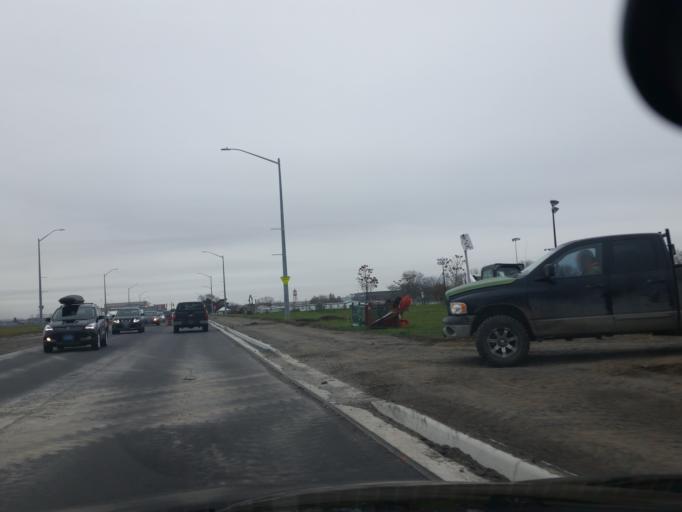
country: CA
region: Ontario
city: Quinte West
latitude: 44.1055
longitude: -77.5513
